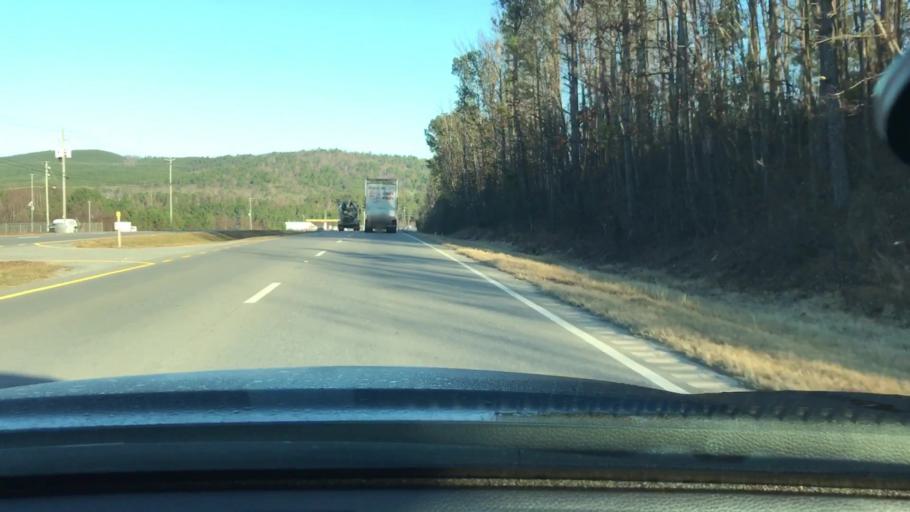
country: US
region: Alabama
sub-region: Talladega County
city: Mignon
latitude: 33.1894
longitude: -86.3053
